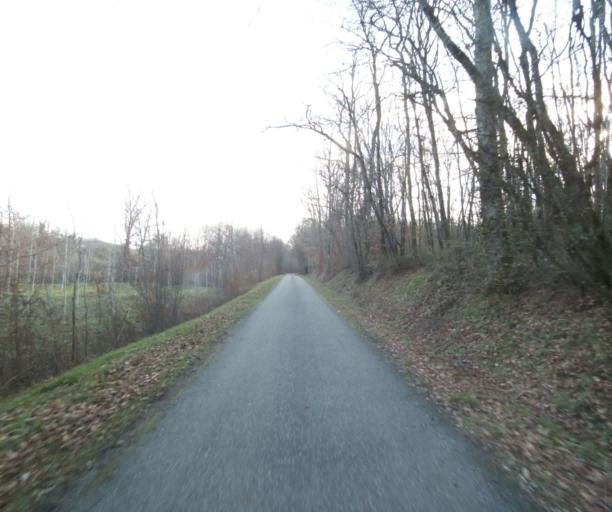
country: FR
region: Midi-Pyrenees
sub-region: Departement du Tarn-et-Garonne
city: Moissac
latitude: 44.1258
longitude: 1.0435
